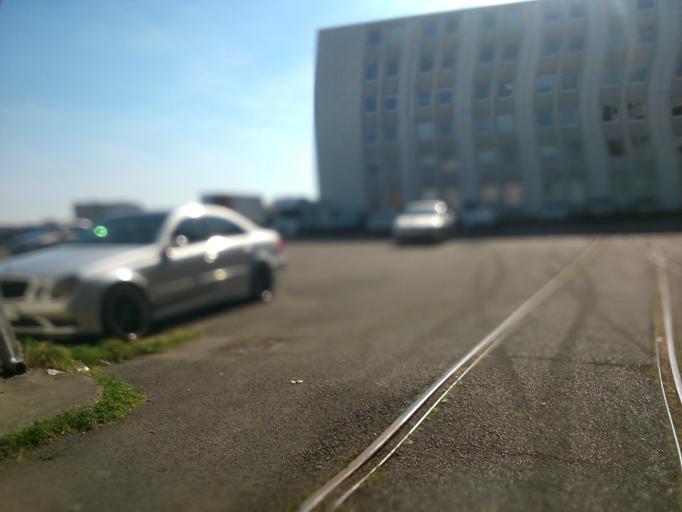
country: FR
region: Pays de la Loire
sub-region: Departement de la Loire-Atlantique
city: Nantes
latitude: 47.1992
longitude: -1.5802
